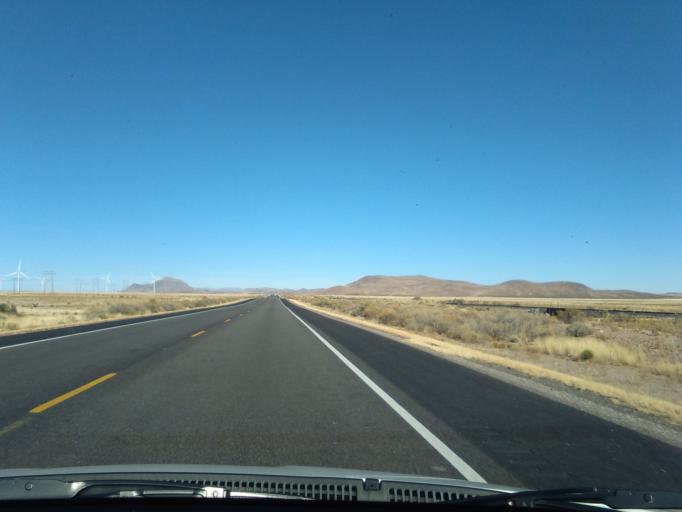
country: US
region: New Mexico
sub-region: Luna County
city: Deming
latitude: 32.5039
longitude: -107.5101
